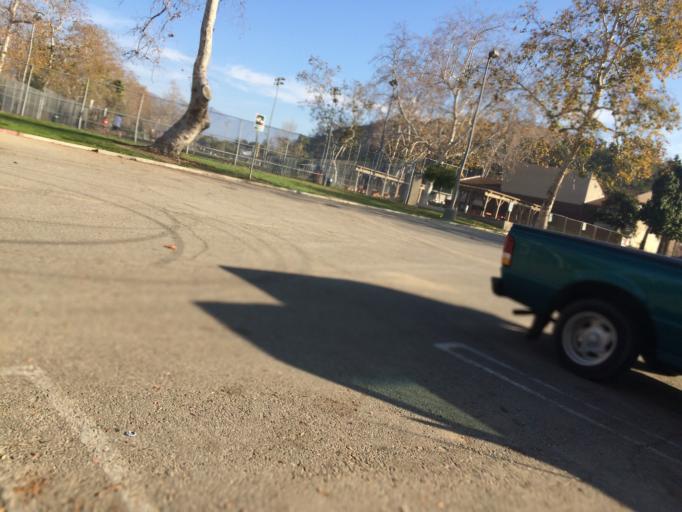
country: US
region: California
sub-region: Los Angeles County
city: South Pasadena
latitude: 34.0954
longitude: -118.2045
